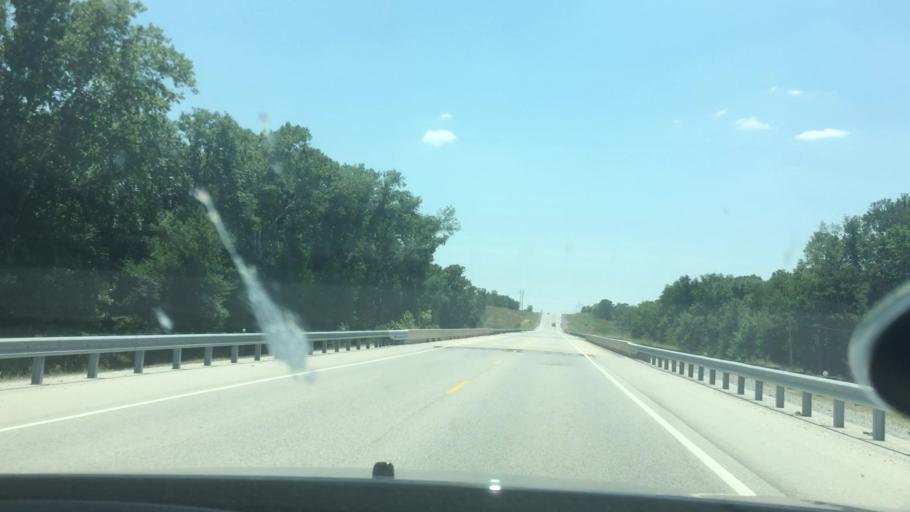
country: US
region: Oklahoma
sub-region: Bryan County
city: Durant
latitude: 34.0922
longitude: -96.3671
